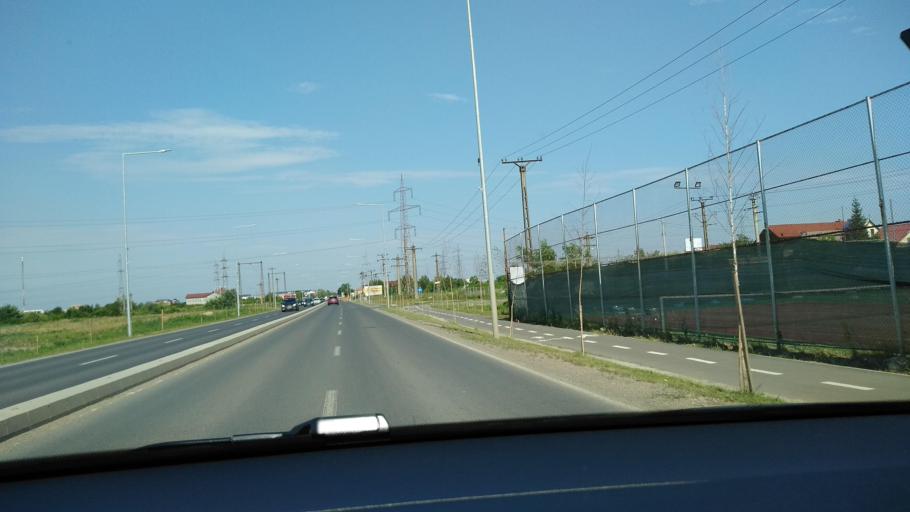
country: RO
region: Timis
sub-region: Comuna Mosnita Noua
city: Mosnita Noua
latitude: 45.7244
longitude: 21.2919
